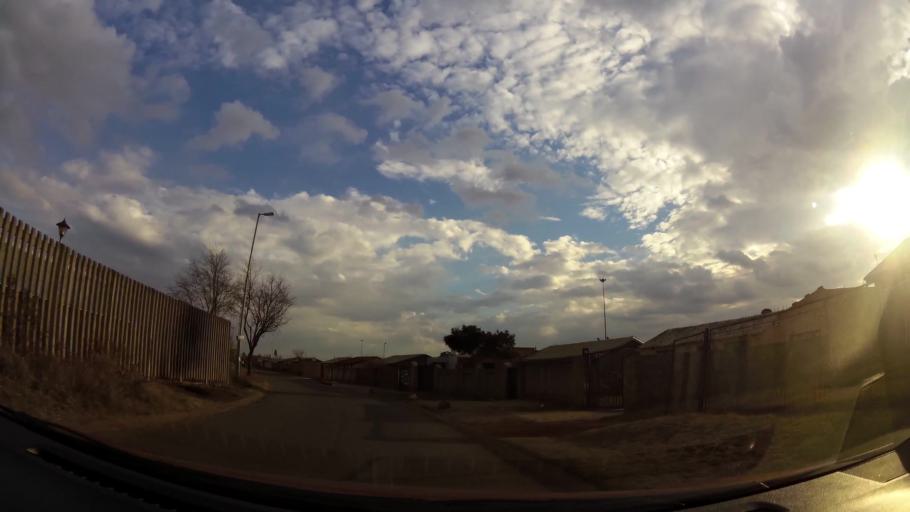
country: ZA
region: Gauteng
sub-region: City of Johannesburg Metropolitan Municipality
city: Soweto
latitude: -26.2385
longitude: 27.8227
